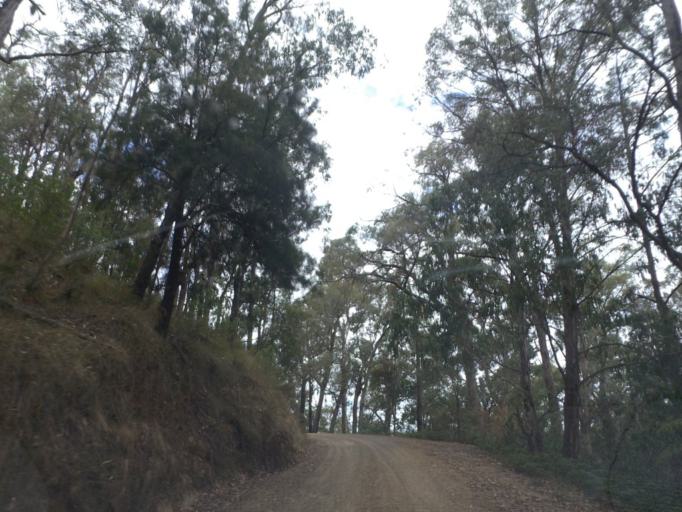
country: AU
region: Victoria
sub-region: Murrindindi
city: Alexandra
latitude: -37.4311
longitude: 145.9715
